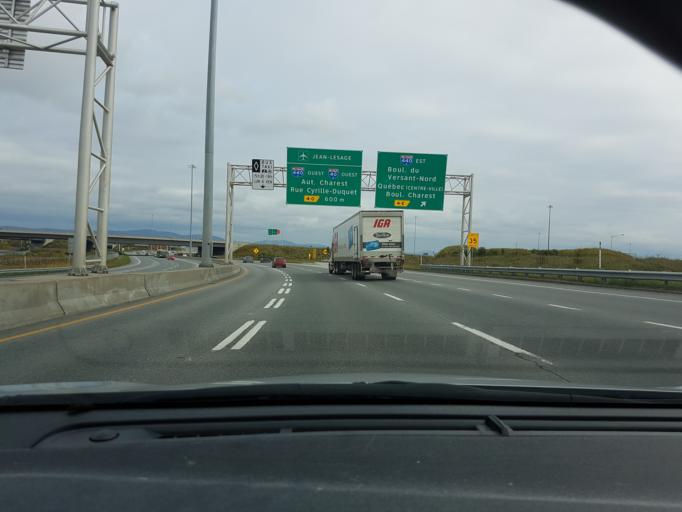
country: CA
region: Quebec
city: L'Ancienne-Lorette
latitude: 46.7916
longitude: -71.2892
